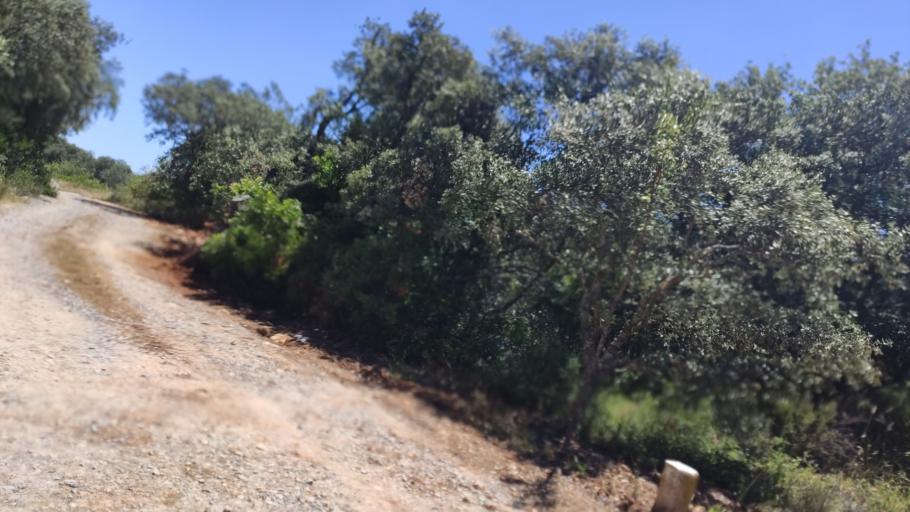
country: PT
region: Faro
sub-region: Sao Bras de Alportel
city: Sao Bras de Alportel
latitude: 37.1607
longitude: -7.9313
